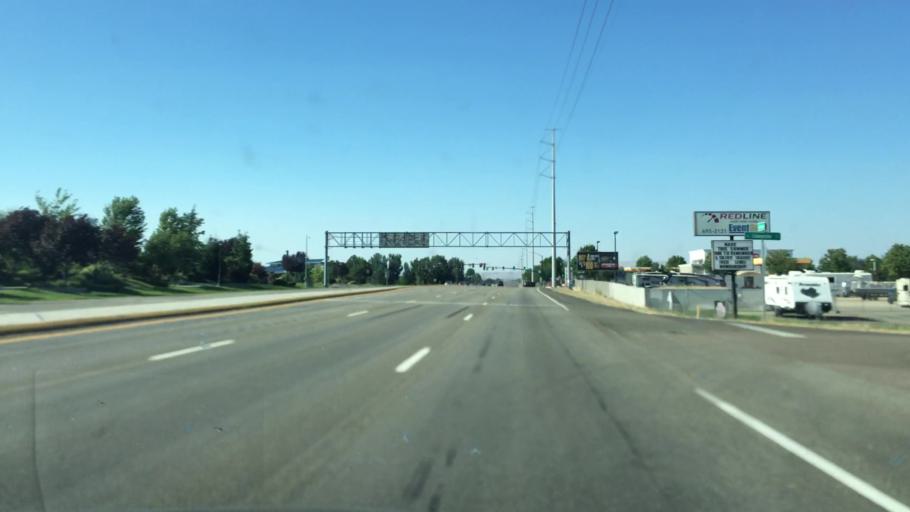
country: US
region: Idaho
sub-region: Ada County
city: Meridian
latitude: 43.6097
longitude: -116.3546
